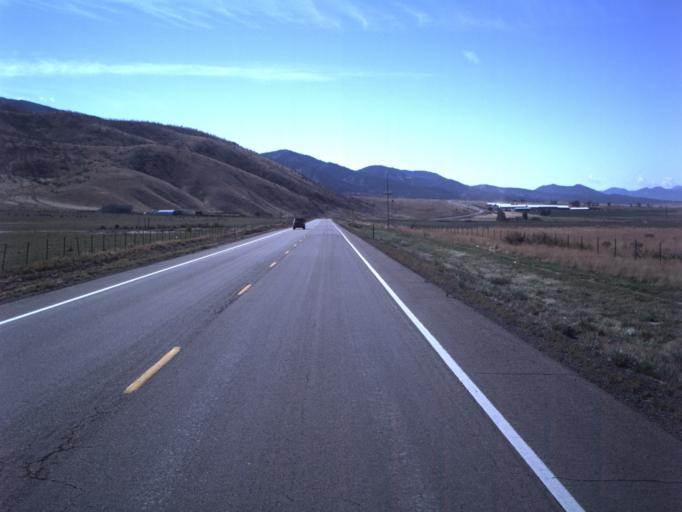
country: US
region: Utah
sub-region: Juab County
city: Nephi
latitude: 39.5415
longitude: -111.8638
